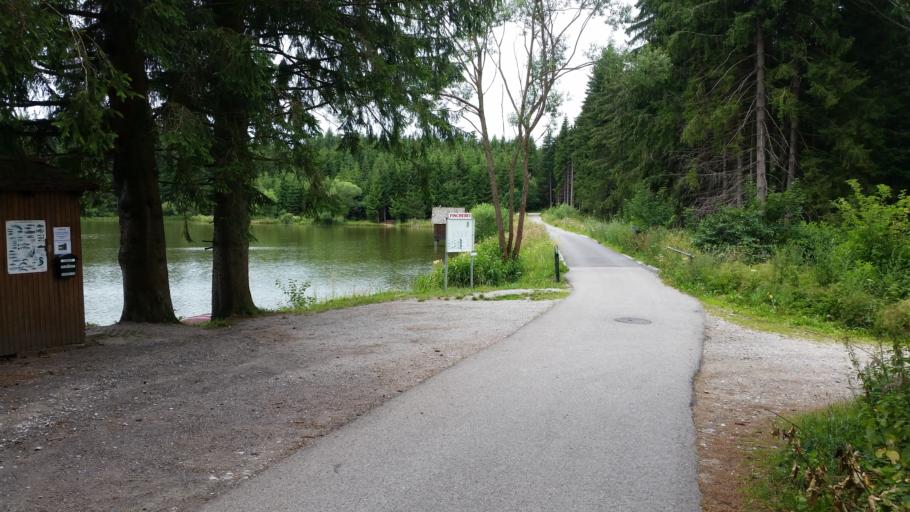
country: AT
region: Lower Austria
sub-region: Politischer Bezirk Zwettl
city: Ottenschlag
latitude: 48.4189
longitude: 15.1796
